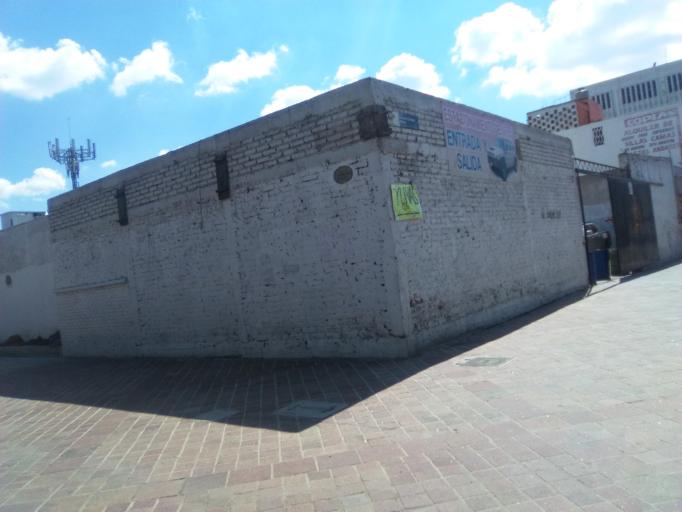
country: MX
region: Guanajuato
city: Leon
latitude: 21.1185
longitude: -101.6712
